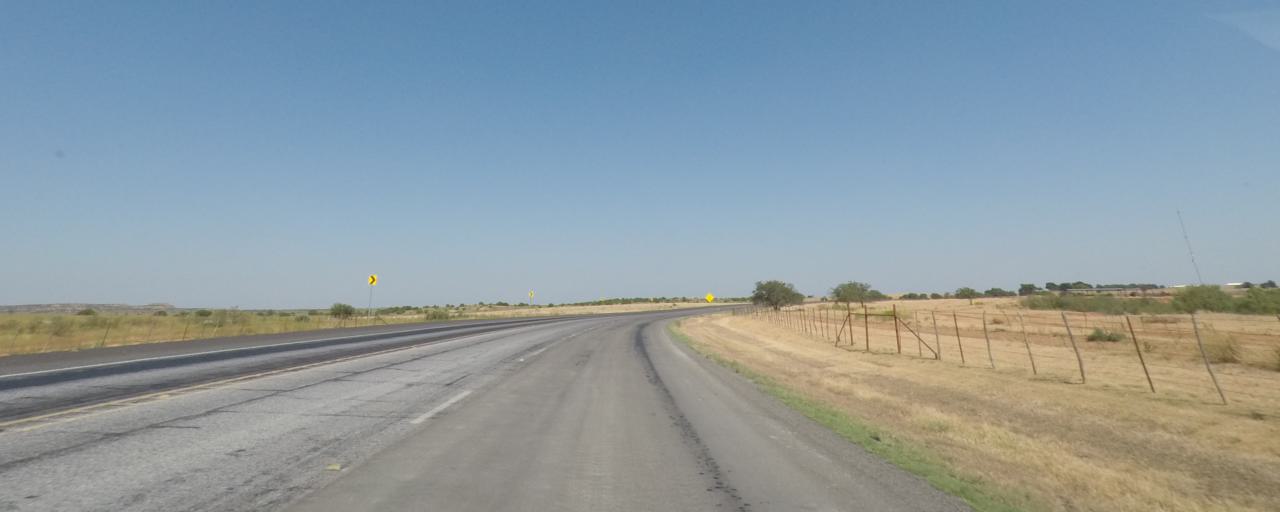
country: US
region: Texas
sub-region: King County
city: Guthrie
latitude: 33.6335
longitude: -100.3454
